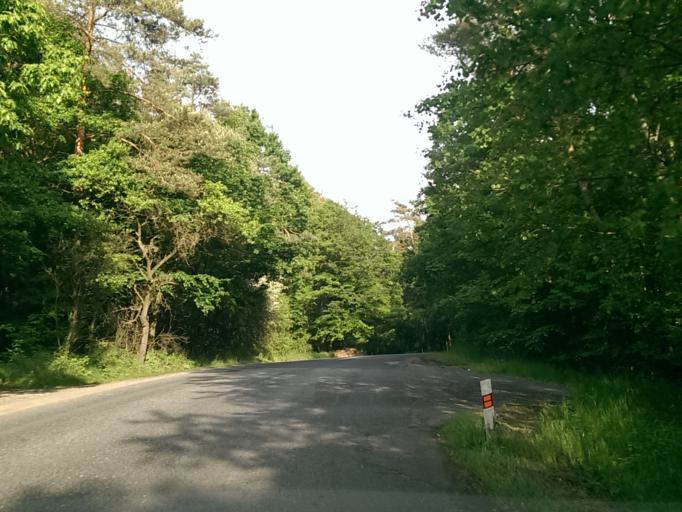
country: CZ
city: Duba
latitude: 50.5551
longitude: 14.5877
